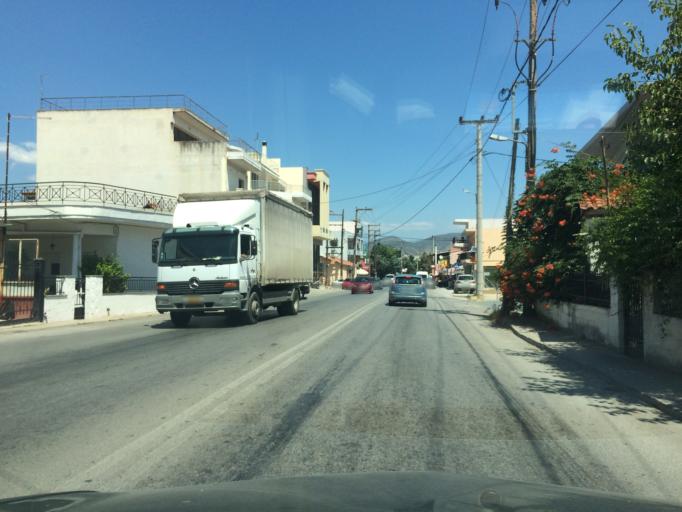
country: GR
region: Central Greece
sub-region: Nomos Evvoias
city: Chalkida
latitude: 38.4614
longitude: 23.6119
